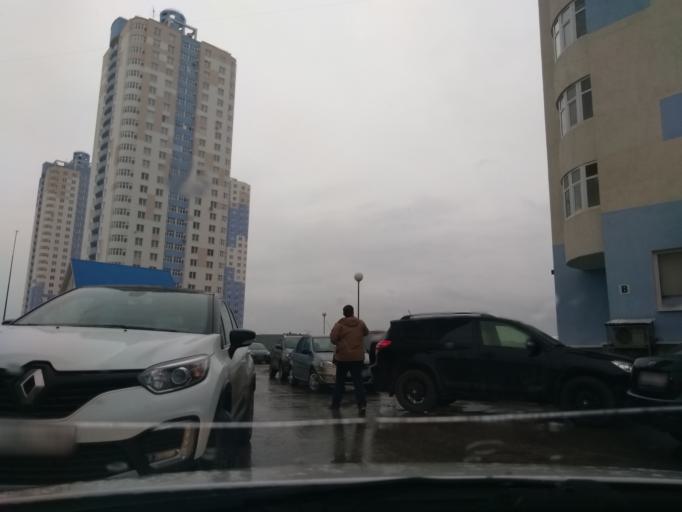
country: RU
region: Perm
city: Perm
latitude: 58.0063
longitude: 56.3217
